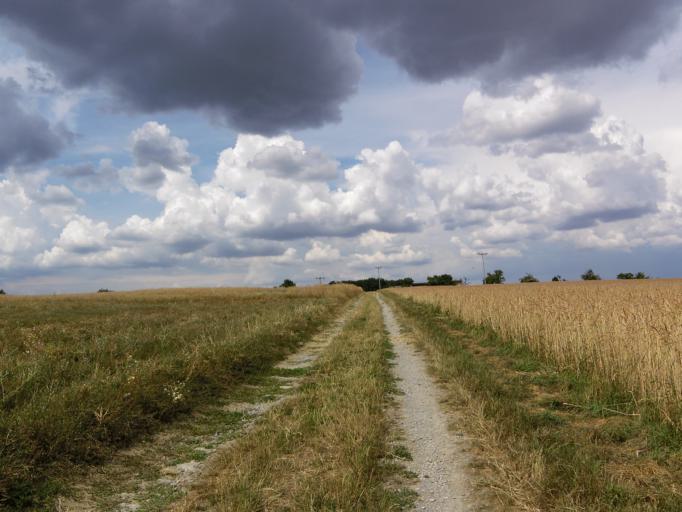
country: DE
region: Bavaria
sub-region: Regierungsbezirk Unterfranken
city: Gerbrunn
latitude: 49.7720
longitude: 9.9833
